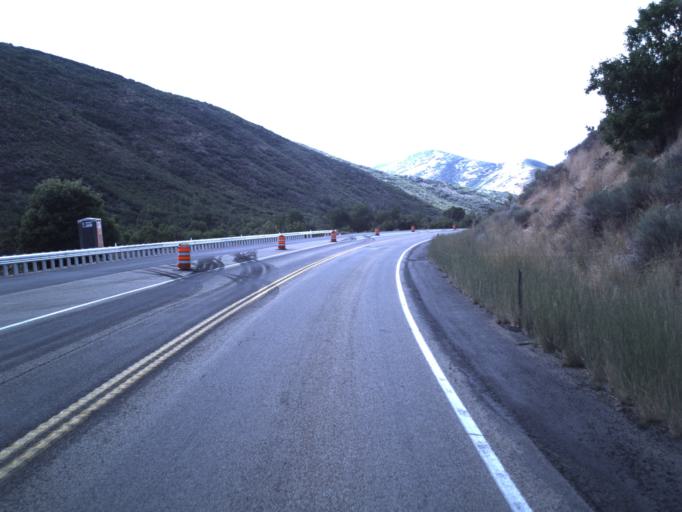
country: US
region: Utah
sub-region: Wasatch County
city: Heber
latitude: 40.4222
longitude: -111.3425
